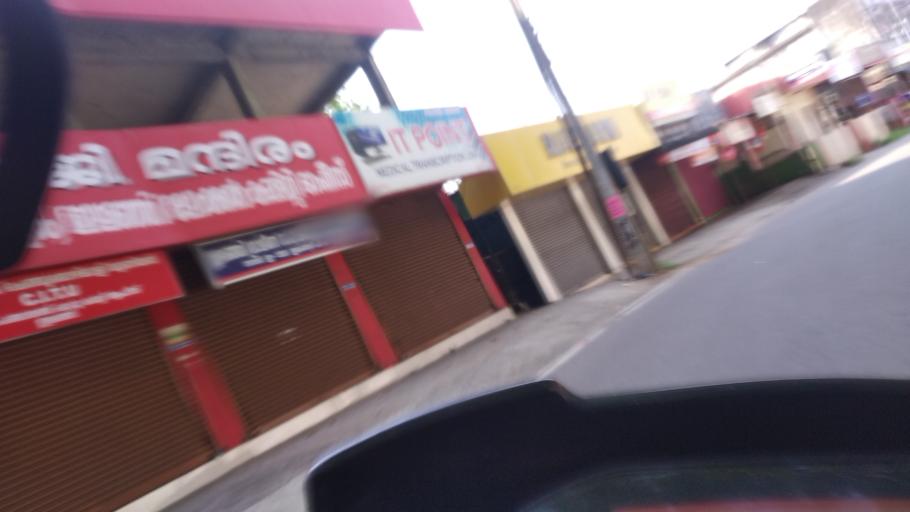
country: IN
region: Kerala
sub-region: Ernakulam
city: Piravam
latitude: 9.8314
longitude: 76.5452
